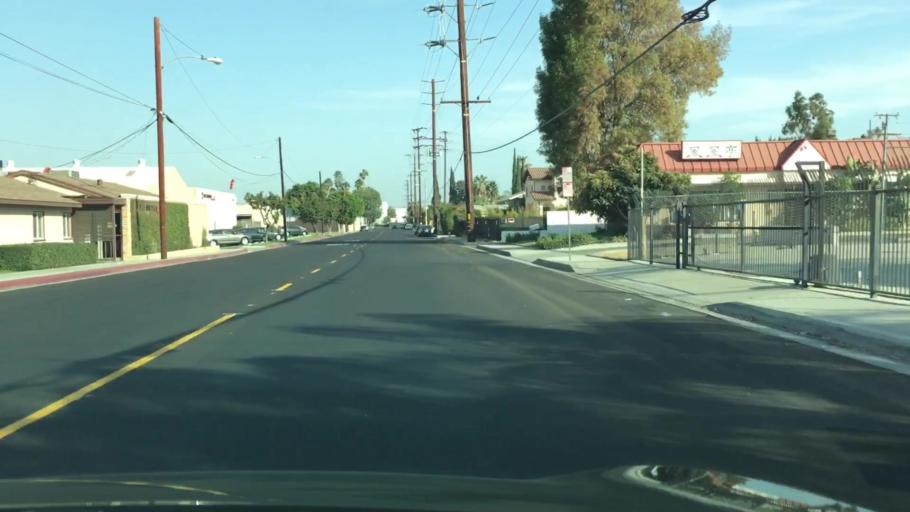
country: US
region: California
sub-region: Los Angeles County
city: Avocado Heights
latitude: 34.0200
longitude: -117.9777
